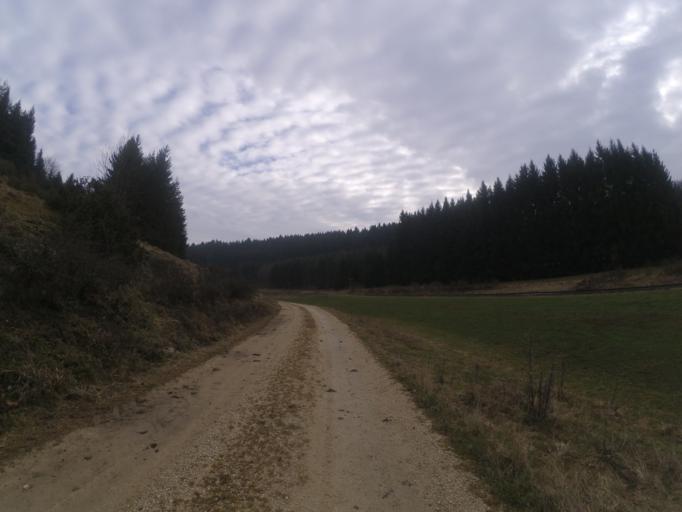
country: DE
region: Baden-Wuerttemberg
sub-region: Tuebingen Region
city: Mehrstetten
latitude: 48.3562
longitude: 9.5468
